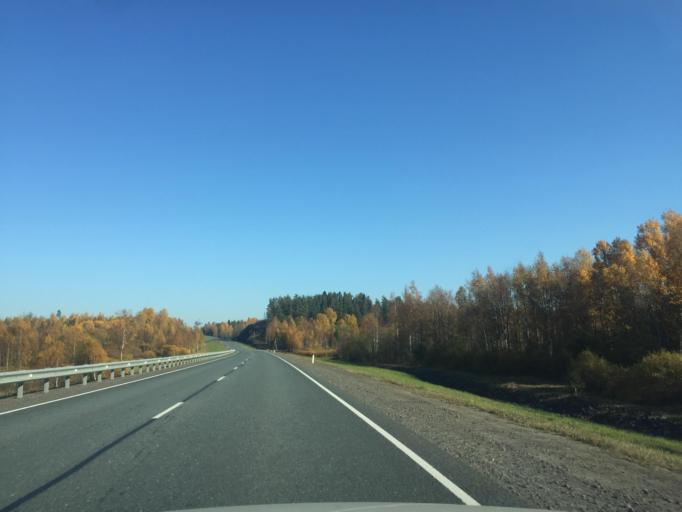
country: RU
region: Leningrad
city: Kuznechnoye
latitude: 61.3466
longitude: 29.8760
